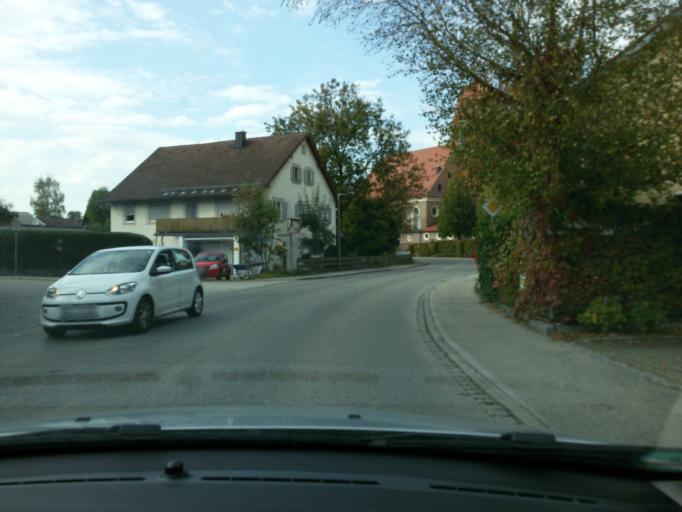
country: DE
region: Bavaria
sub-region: Swabia
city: Buchloe
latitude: 48.0363
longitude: 10.7311
